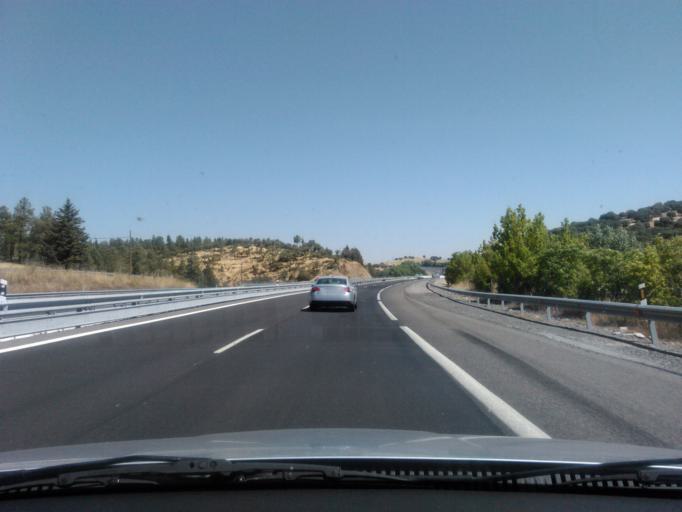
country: ES
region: Castille-La Mancha
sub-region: Provincia de Ciudad Real
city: Viso del Marques
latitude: 38.4446
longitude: -3.4965
